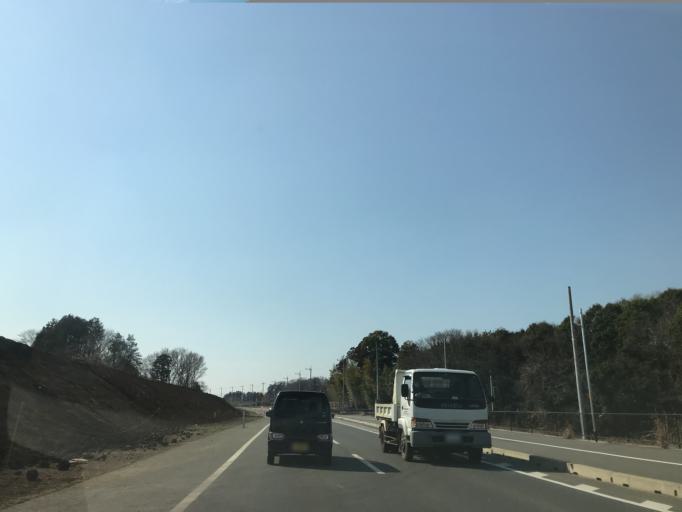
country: JP
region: Ibaraki
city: Mitsukaido
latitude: 36.0129
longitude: 140.0350
